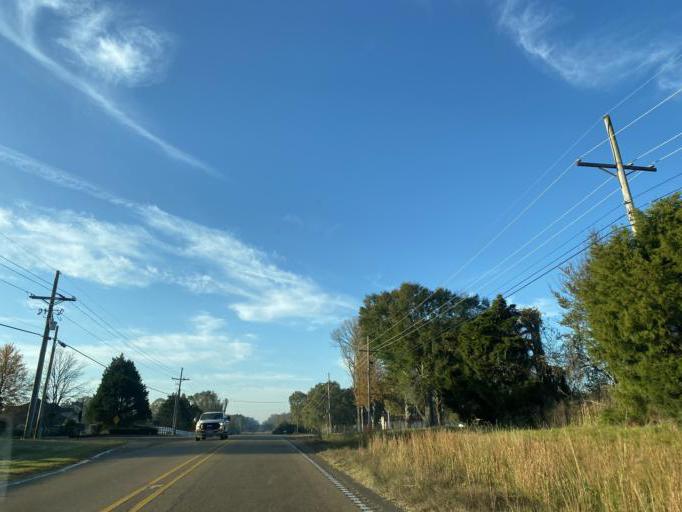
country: US
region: Mississippi
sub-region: Madison County
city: Madison
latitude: 32.5040
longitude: -90.0895
